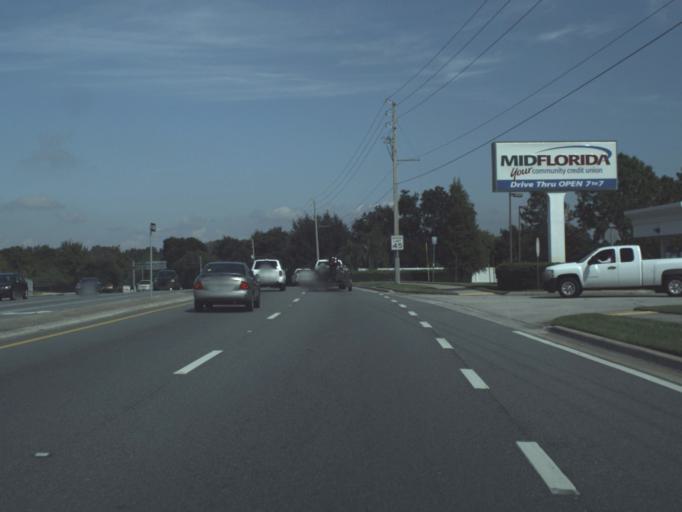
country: US
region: Florida
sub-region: Polk County
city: Cypress Gardens
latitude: 27.9972
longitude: -81.6887
